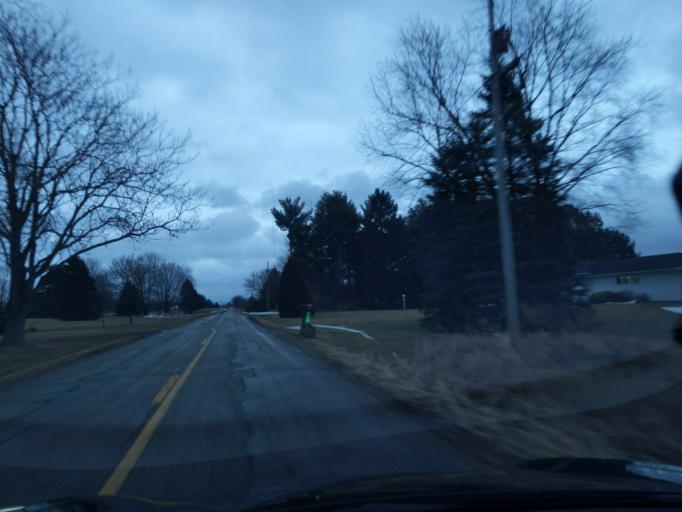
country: US
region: Michigan
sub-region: Eaton County
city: Eaton Rapids
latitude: 42.4437
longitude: -84.5934
